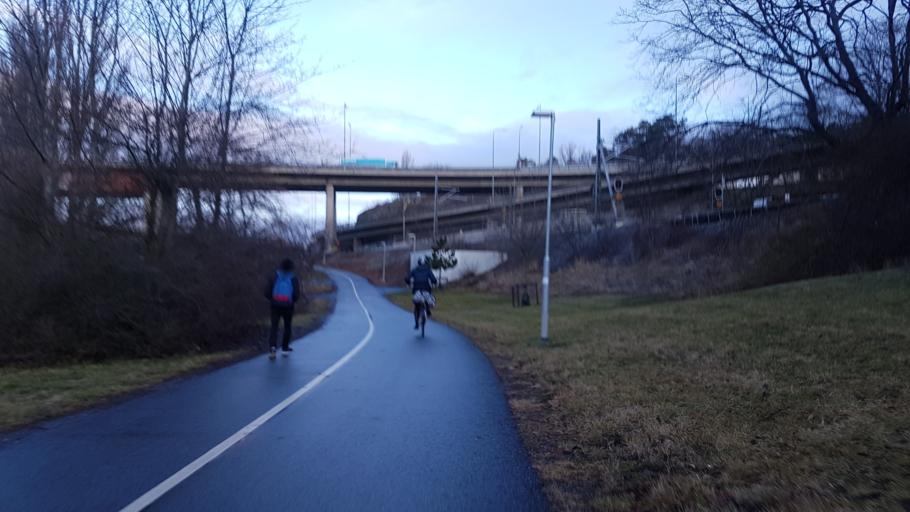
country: SE
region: Stockholm
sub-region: Lidingo
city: Lidingoe
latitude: 59.3618
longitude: 18.1173
